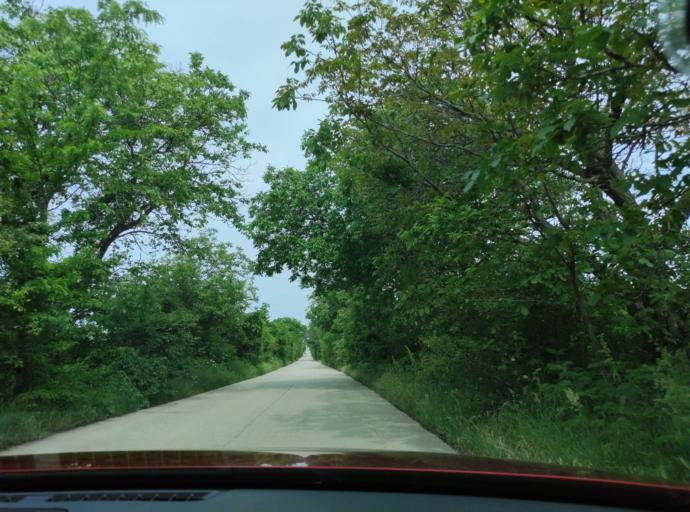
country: BG
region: Pleven
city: Iskur
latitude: 43.5224
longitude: 24.3237
